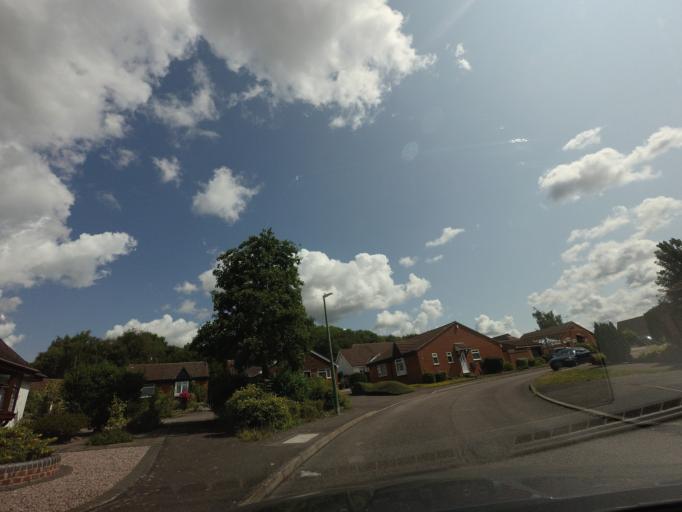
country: GB
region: England
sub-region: Kent
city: Boxley
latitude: 51.2757
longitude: 0.5530
